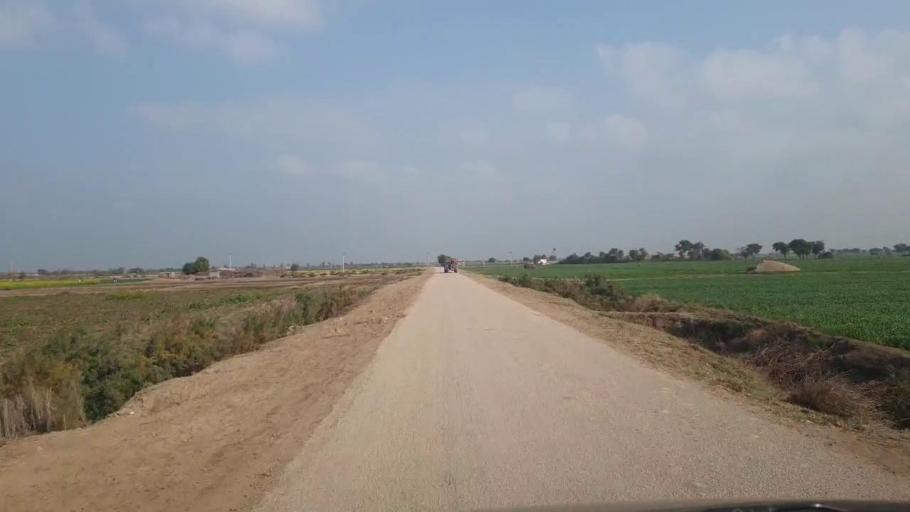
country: PK
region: Sindh
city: Shahdadpur
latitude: 25.9074
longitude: 68.6638
